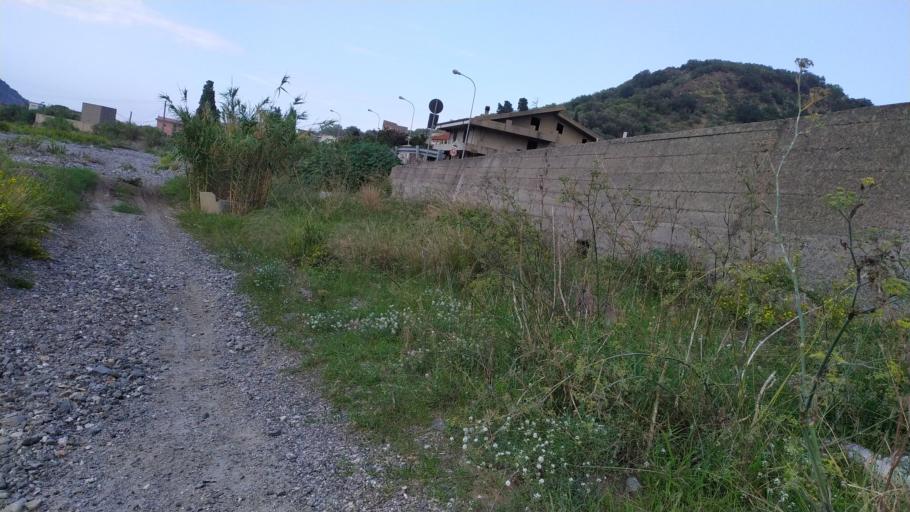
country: IT
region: Sicily
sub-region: Messina
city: Saponara
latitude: 38.2018
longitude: 15.4306
